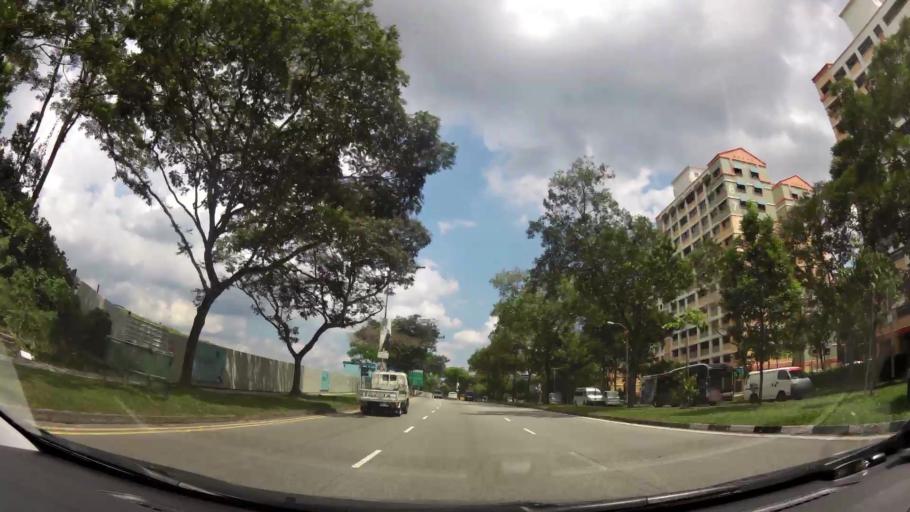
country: MY
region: Johor
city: Johor Bahru
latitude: 1.4453
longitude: 103.7906
